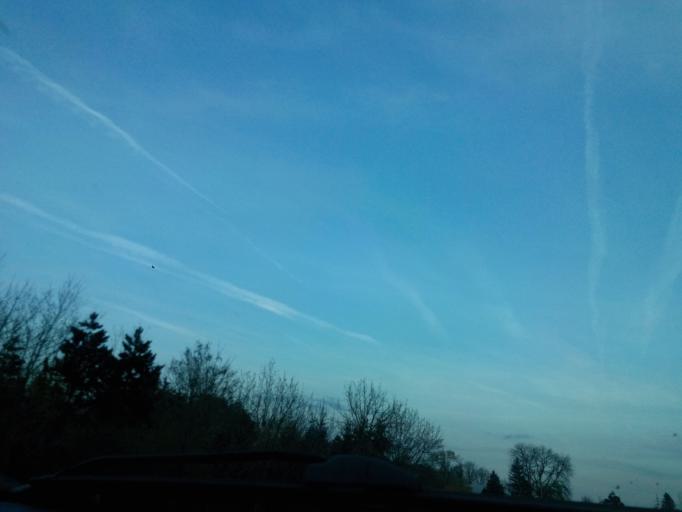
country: RO
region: Prahova
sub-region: Comuna Poiana Campina
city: Bobolia
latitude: 45.1088
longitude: 25.7402
